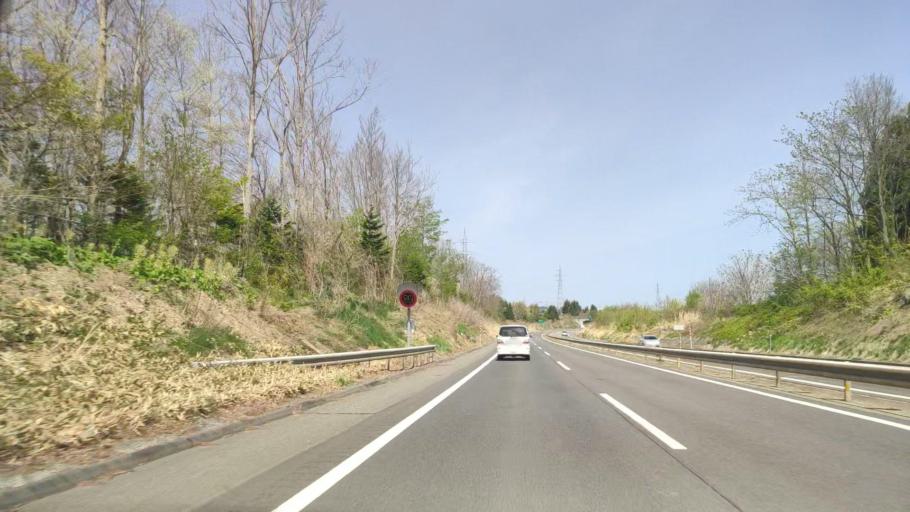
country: JP
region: Aomori
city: Hachinohe
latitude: 40.4737
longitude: 141.4607
